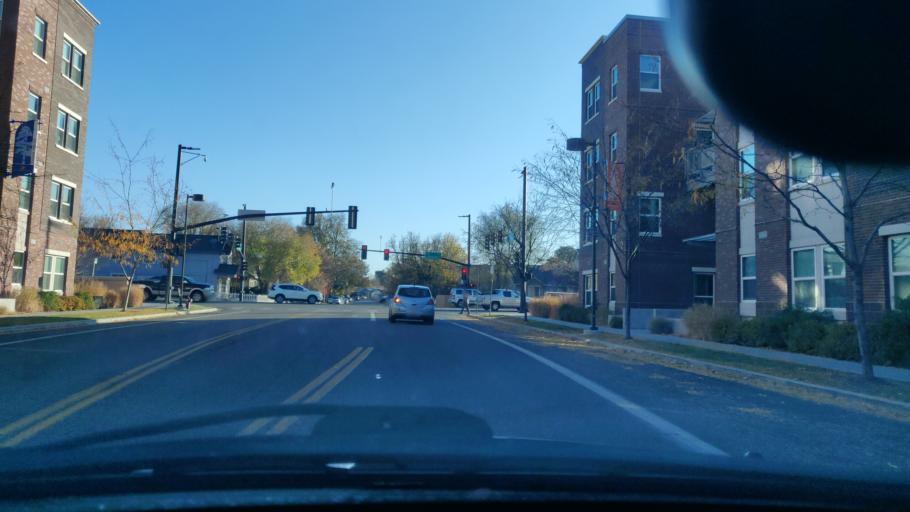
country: US
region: Idaho
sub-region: Ada County
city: Boise
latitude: 43.5990
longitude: -116.2024
